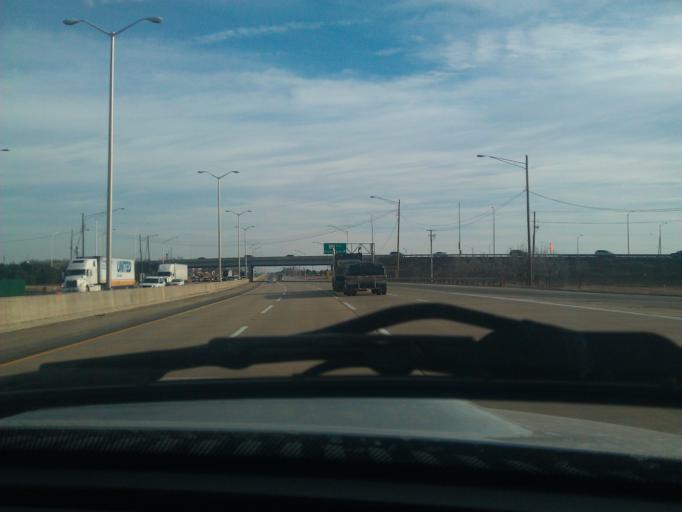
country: US
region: Illinois
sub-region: Lake County
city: Grandwood Park
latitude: 42.3833
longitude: -87.9487
